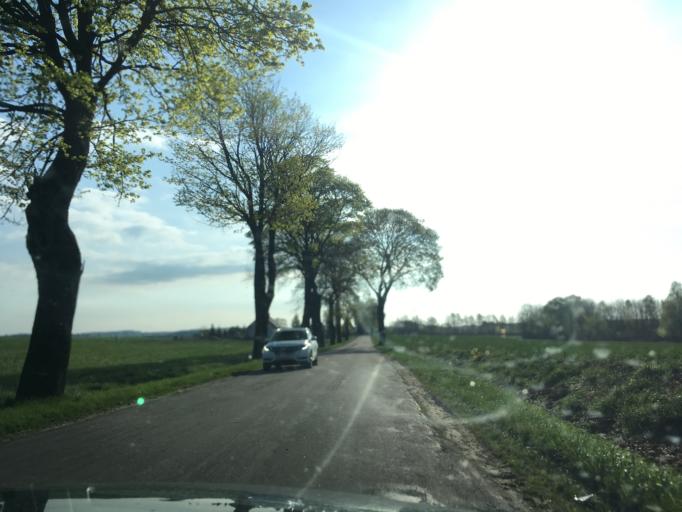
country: PL
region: Warmian-Masurian Voivodeship
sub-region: Powiat nidzicki
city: Kozlowo
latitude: 53.4050
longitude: 20.2890
